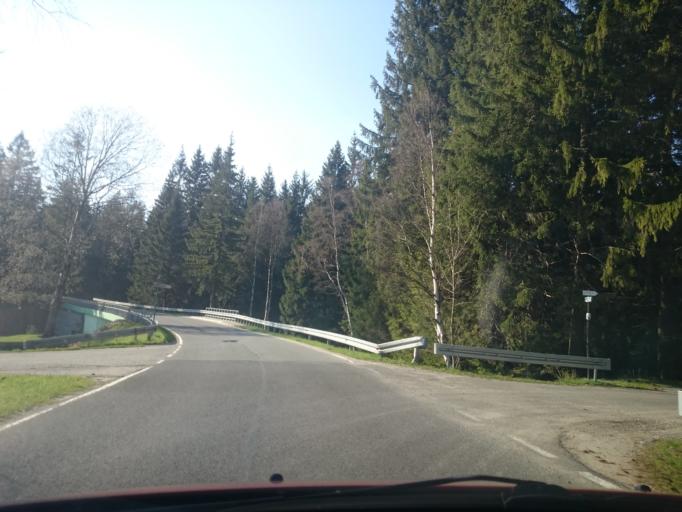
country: PL
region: Lower Silesian Voivodeship
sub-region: Powiat klodzki
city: Szczytna
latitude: 50.3214
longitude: 16.4396
